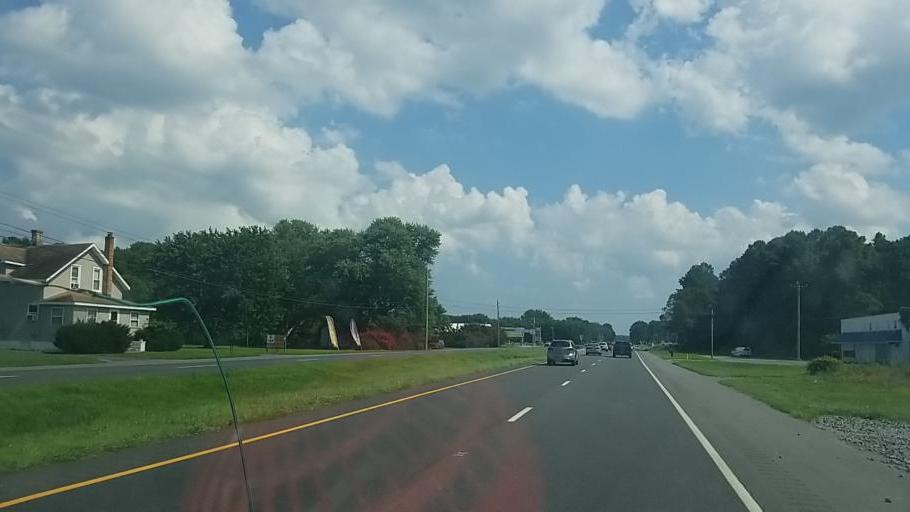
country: US
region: Delaware
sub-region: Sussex County
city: Millsboro
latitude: 38.5367
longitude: -75.2538
